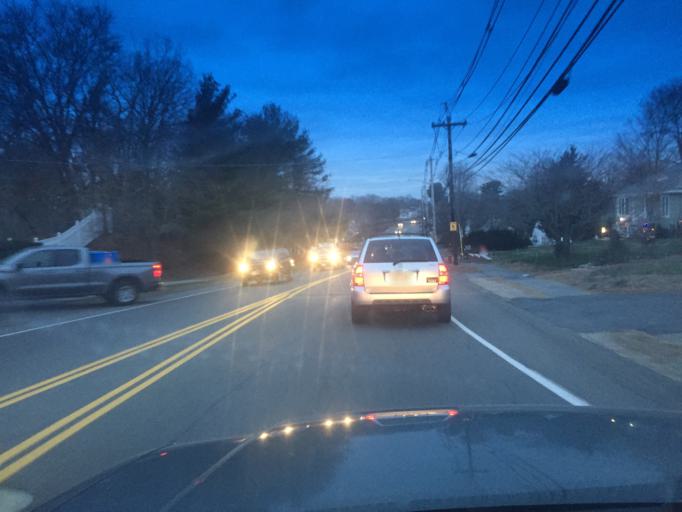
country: US
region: Massachusetts
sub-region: Norfolk County
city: Norwood
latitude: 42.1785
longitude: -71.1805
